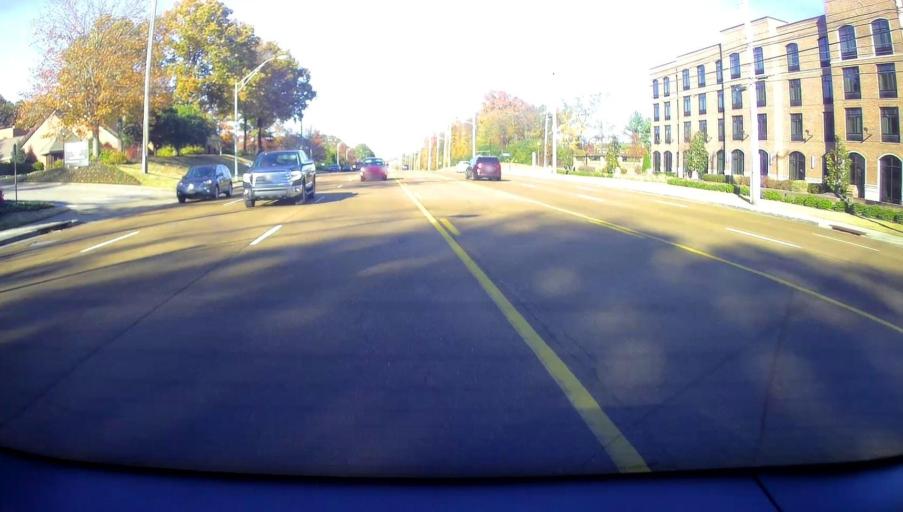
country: US
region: Tennessee
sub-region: Shelby County
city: Germantown
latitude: 35.1031
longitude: -89.8047
